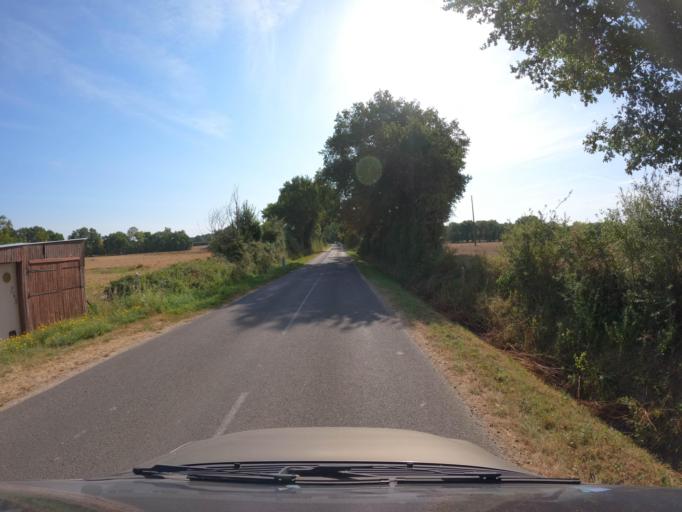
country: FR
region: Pays de la Loire
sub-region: Departement de la Vendee
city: Soullans
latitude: 46.8049
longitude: -1.8864
